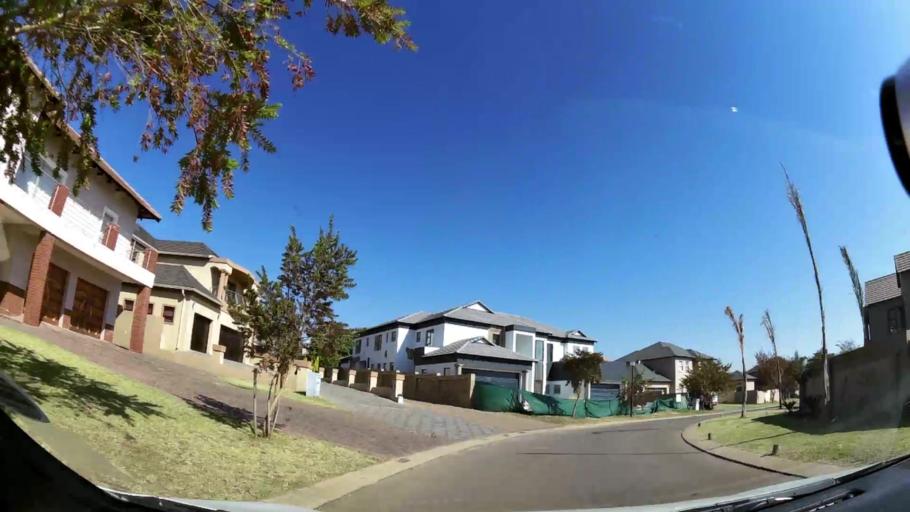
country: ZA
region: Gauteng
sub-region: City of Johannesburg Metropolitan Municipality
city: Midrand
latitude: -25.9351
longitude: 28.1364
